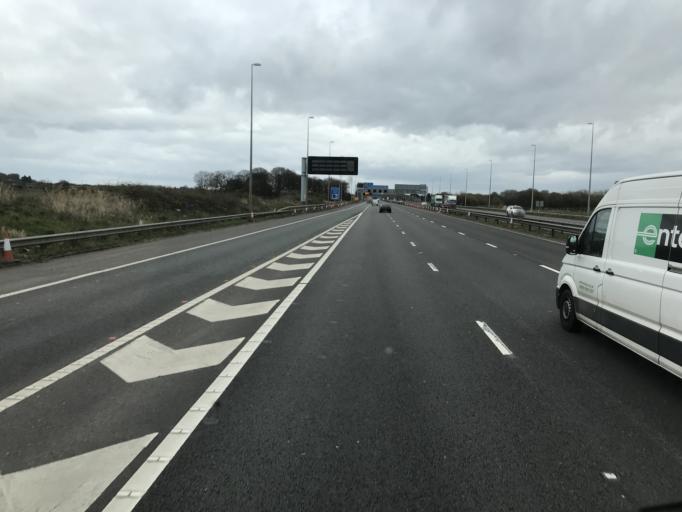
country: GB
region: England
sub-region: Warrington
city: Winwick
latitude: 53.4231
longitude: -2.5913
